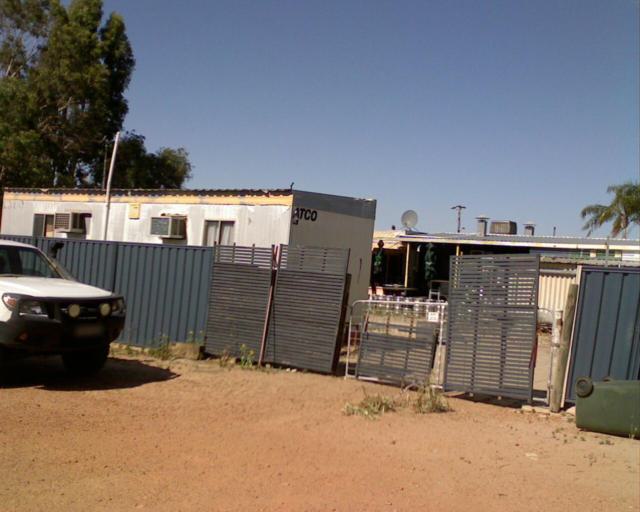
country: AU
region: Western Australia
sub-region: Dandaragan
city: Jurien Bay
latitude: -29.8200
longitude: 115.2668
